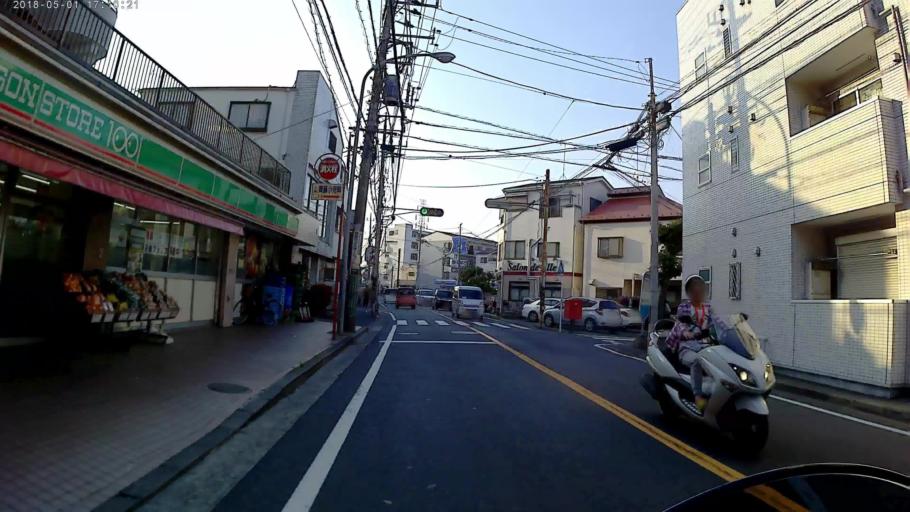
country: JP
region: Kanagawa
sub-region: Kawasaki-shi
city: Kawasaki
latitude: 35.5455
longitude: 139.6253
